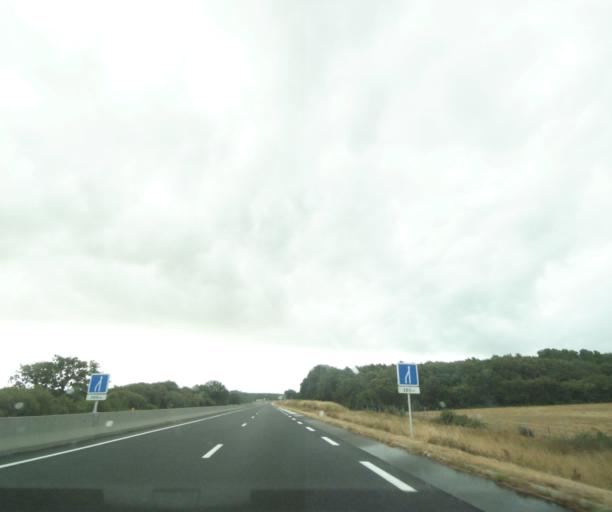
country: FR
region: Pays de la Loire
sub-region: Departement de la Vendee
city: Chateau-d'Olonne
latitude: 46.4859
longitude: -1.7060
